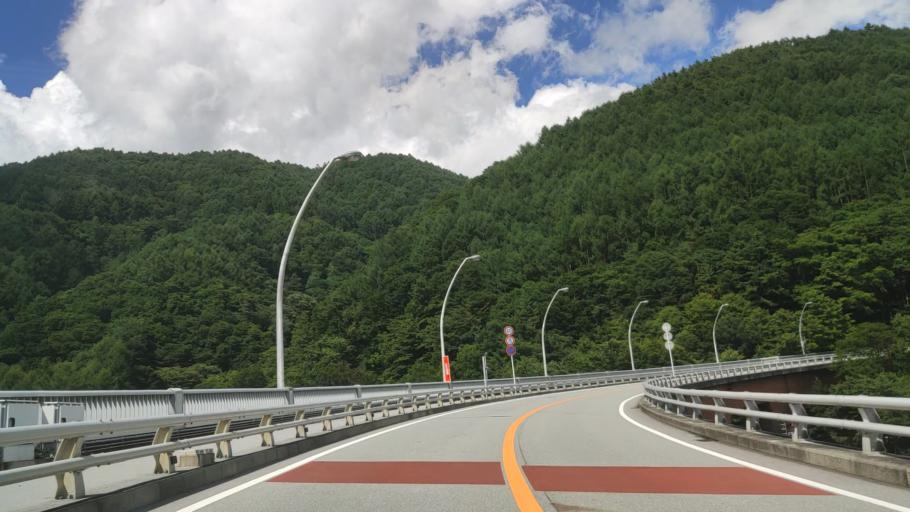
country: JP
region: Yamanashi
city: Enzan
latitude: 35.8631
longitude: 138.7542
